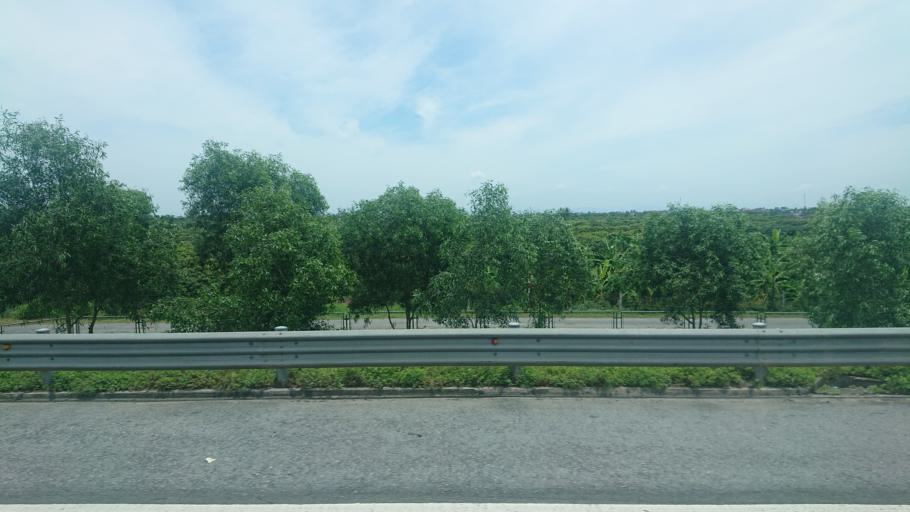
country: VN
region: Hai Duong
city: Tu Ky
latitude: 20.8239
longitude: 106.4683
